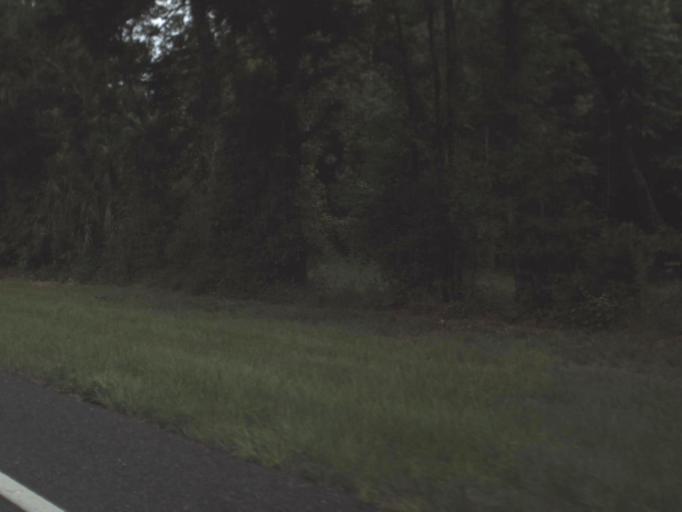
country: US
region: Florida
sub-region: Levy County
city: Bronson
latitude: 29.2668
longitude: -82.7319
